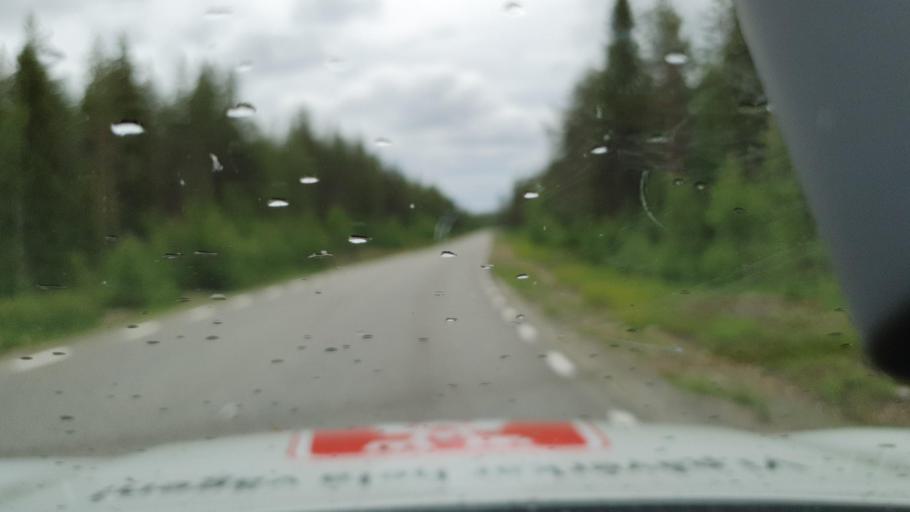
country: SE
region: Vaesterbotten
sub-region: Lycksele Kommun
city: Lycksele
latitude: 64.2310
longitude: 18.2415
